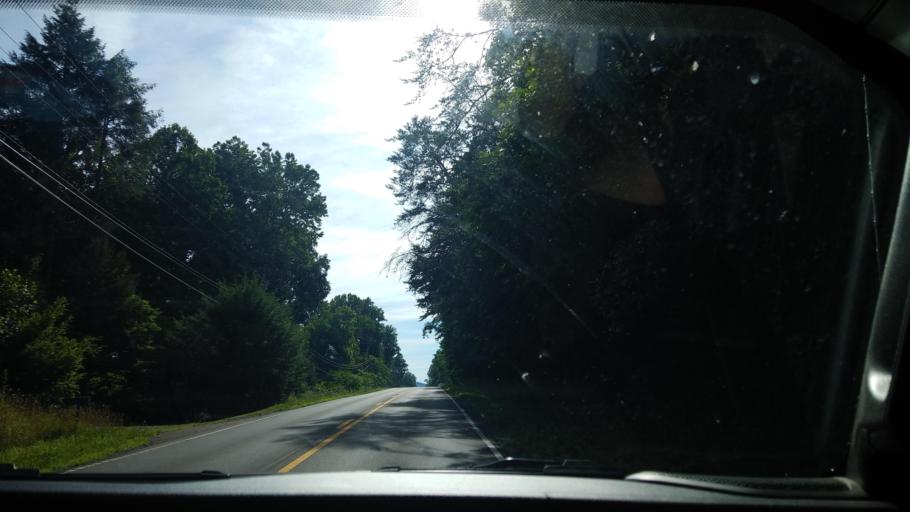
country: US
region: Tennessee
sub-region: Sevier County
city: Gatlinburg
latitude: 35.7586
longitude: -83.3538
